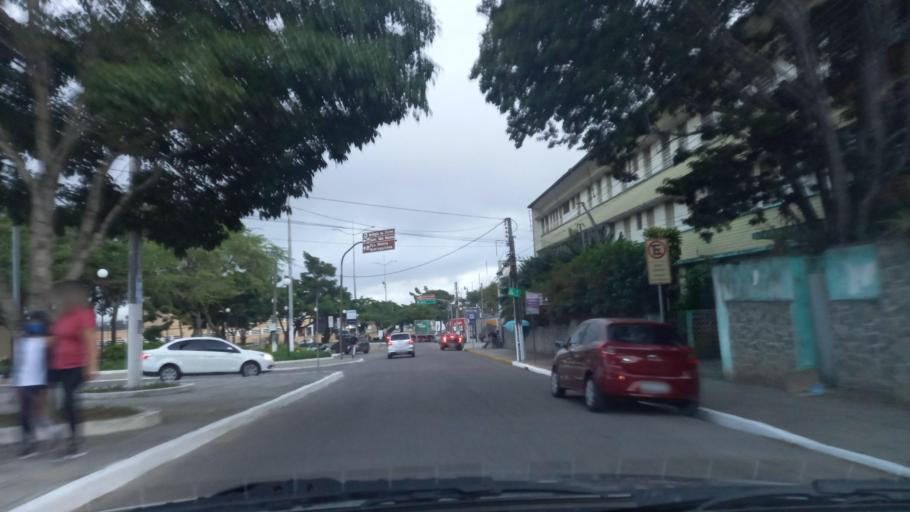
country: BR
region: Pernambuco
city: Garanhuns
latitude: -8.8808
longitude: -36.4768
